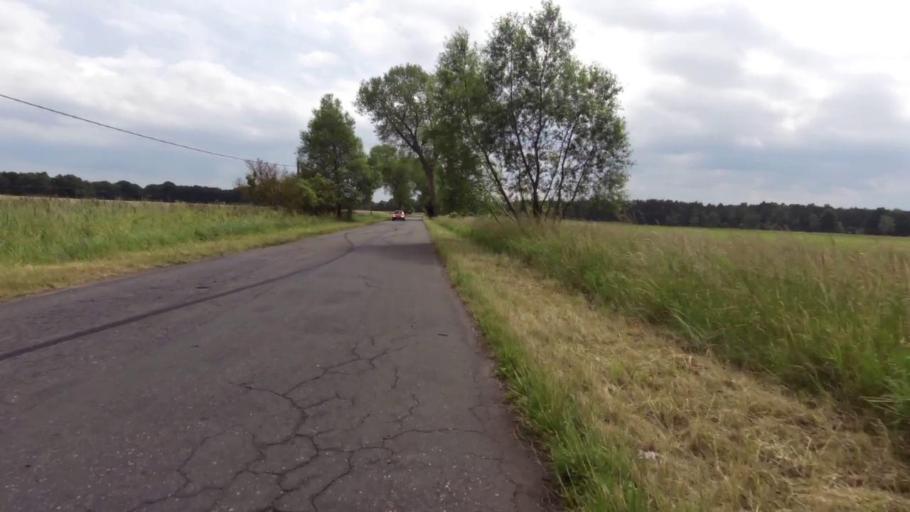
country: PL
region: West Pomeranian Voivodeship
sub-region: Powiat goleniowski
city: Stepnica
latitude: 53.7186
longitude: 14.5549
